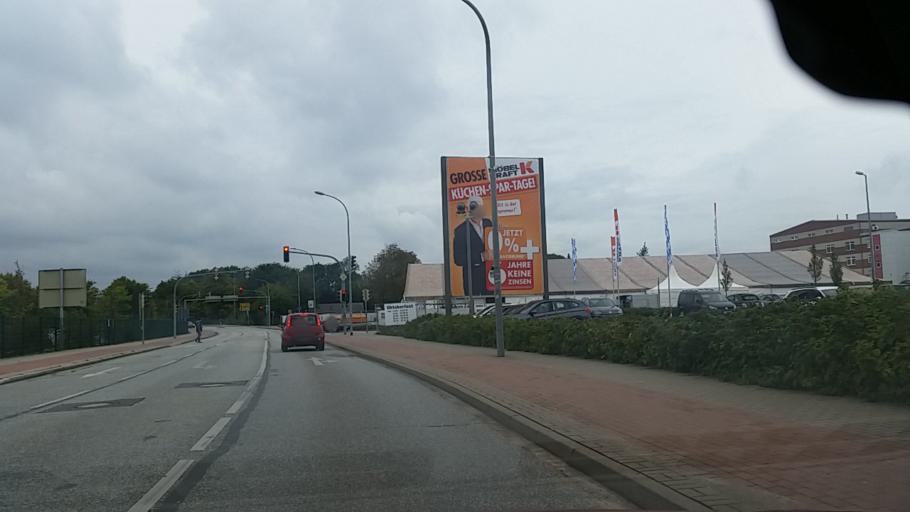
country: DE
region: Schleswig-Holstein
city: Bad Segeberg
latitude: 53.9372
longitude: 10.2980
